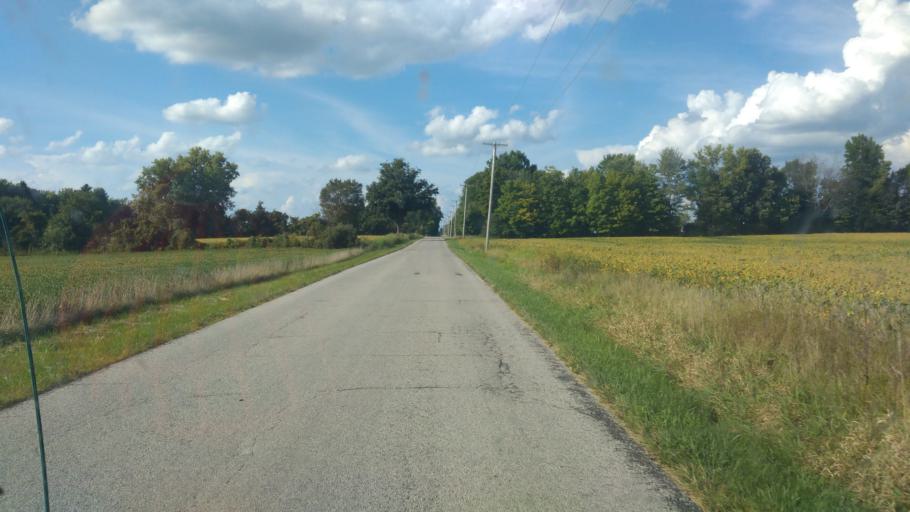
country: US
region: Ohio
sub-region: Crawford County
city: Galion
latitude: 40.7472
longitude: -82.7745
